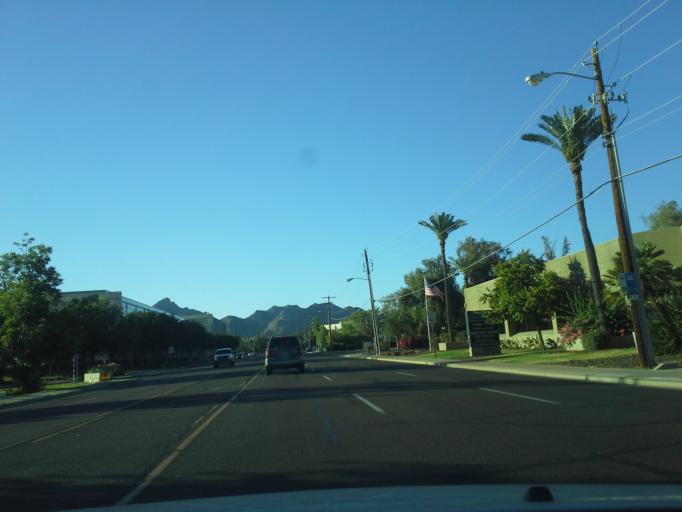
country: US
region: Arizona
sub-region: Maricopa County
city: Paradise Valley
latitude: 33.5066
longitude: -112.0130
